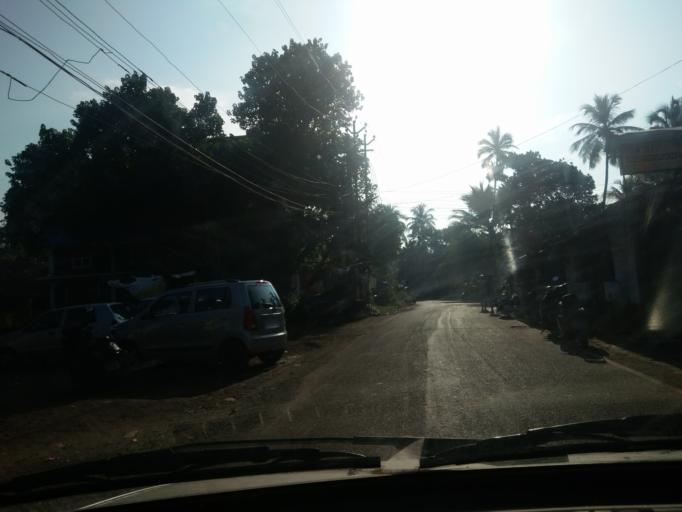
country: IN
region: Goa
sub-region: South Goa
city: Cuncolim
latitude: 15.1803
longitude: 73.9720
